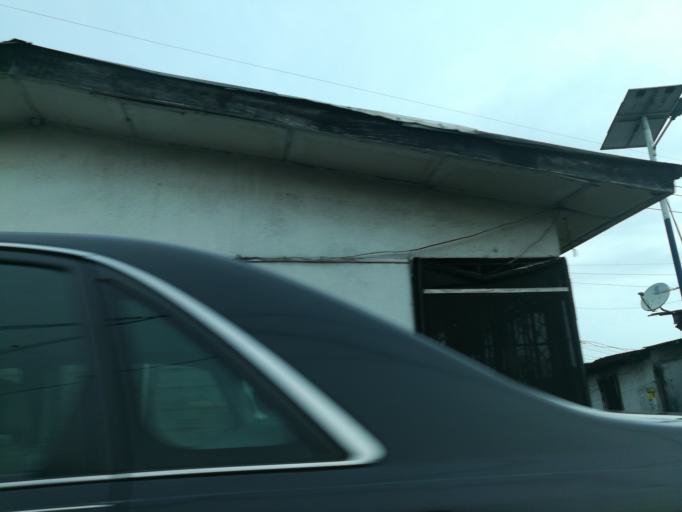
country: NG
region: Rivers
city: Port Harcourt
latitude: 4.8116
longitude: 7.0196
